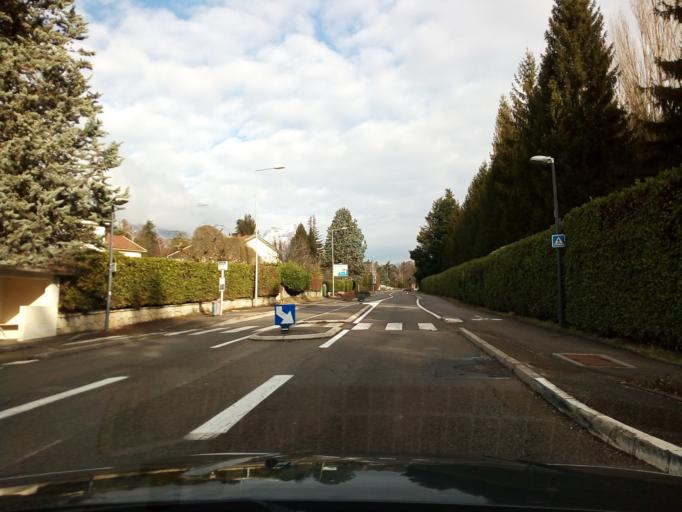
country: FR
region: Rhone-Alpes
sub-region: Departement de l'Isere
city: Meylan
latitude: 45.2186
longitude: 5.7867
